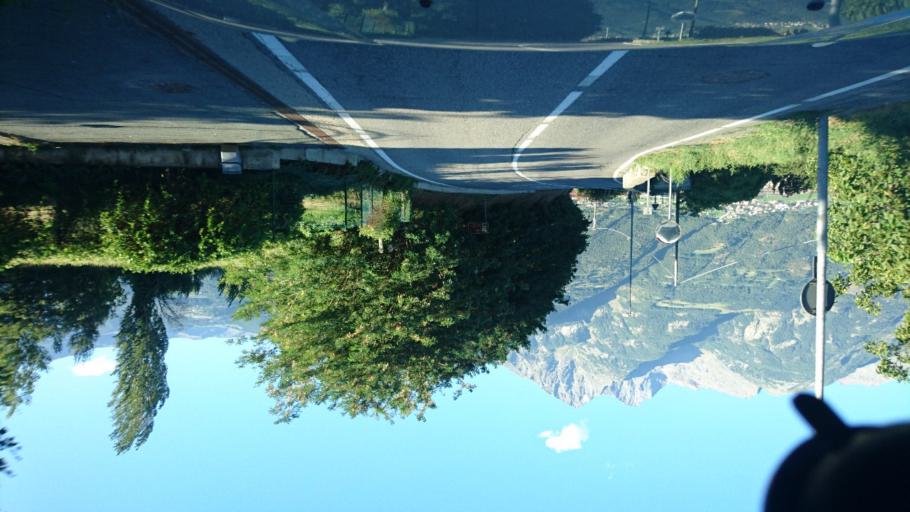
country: IT
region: Aosta Valley
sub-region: Valle d'Aosta
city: Aosta
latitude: 45.7466
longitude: 7.3214
